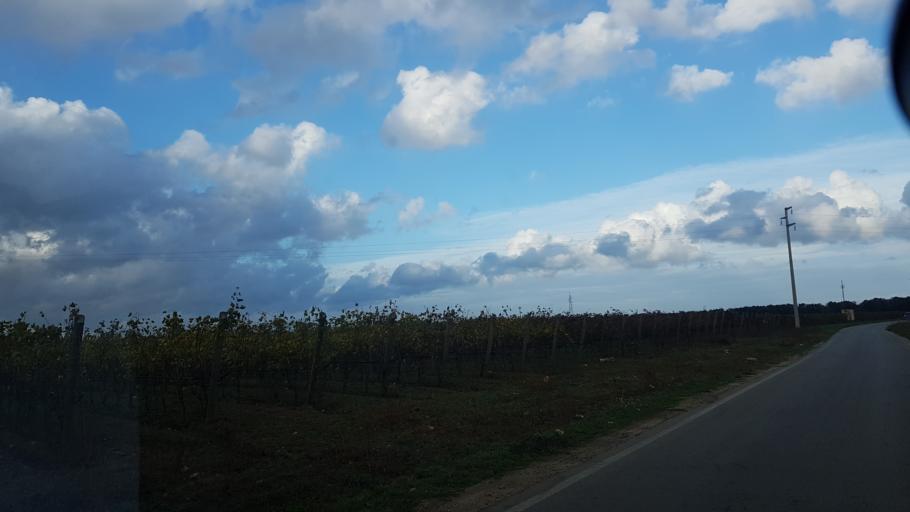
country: IT
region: Apulia
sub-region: Provincia di Brindisi
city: San Pietro Vernotico
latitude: 40.5067
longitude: 18.0173
